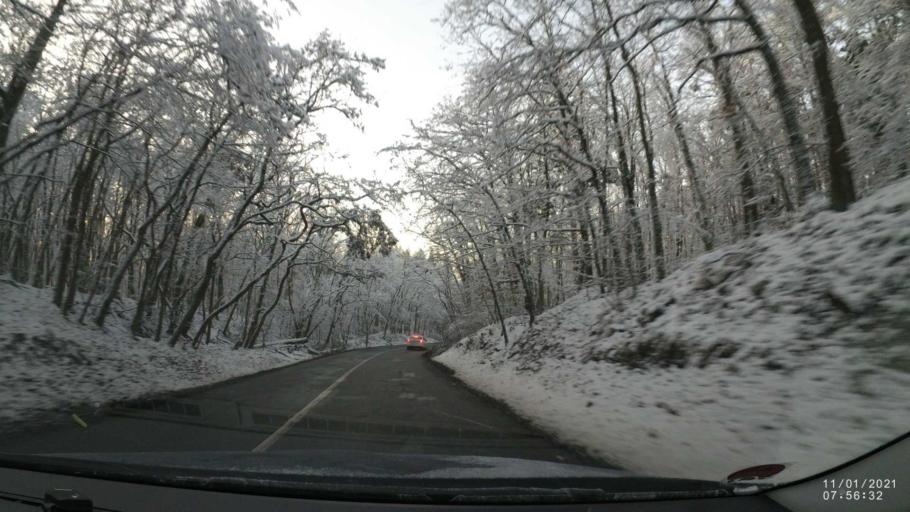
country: CZ
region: South Moravian
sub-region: Okres Blansko
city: Adamov
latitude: 49.2728
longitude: 16.6302
